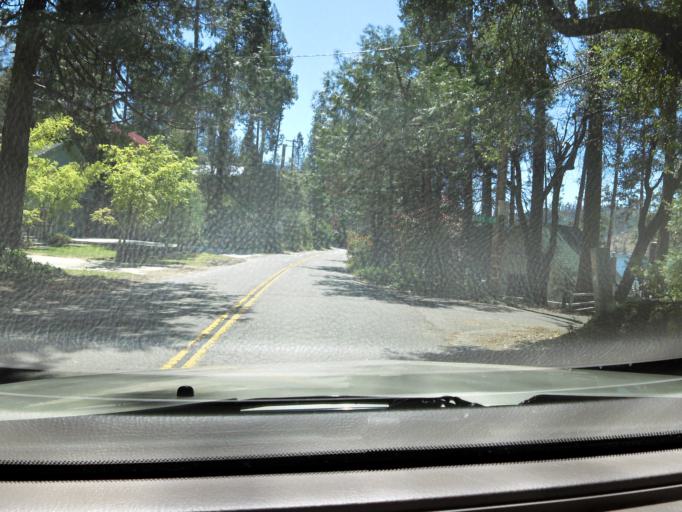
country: US
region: California
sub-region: Madera County
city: Oakhurst
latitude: 37.3278
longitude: -119.5702
